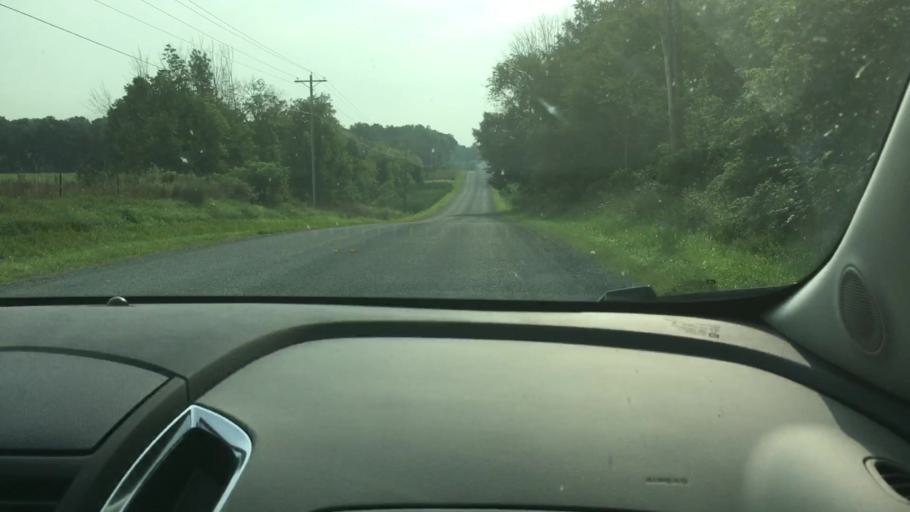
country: US
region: Michigan
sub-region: Cass County
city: Marcellus
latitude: 42.0269
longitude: -85.7853
